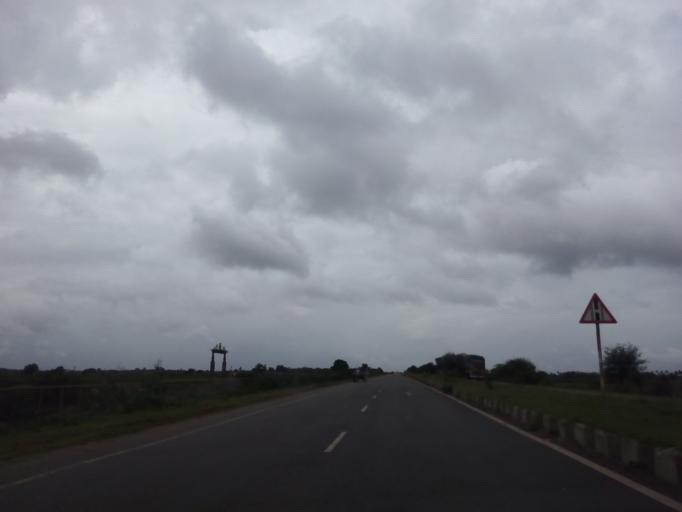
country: IN
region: Karnataka
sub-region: Haveri
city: Haveri
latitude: 14.7484
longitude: 75.4519
